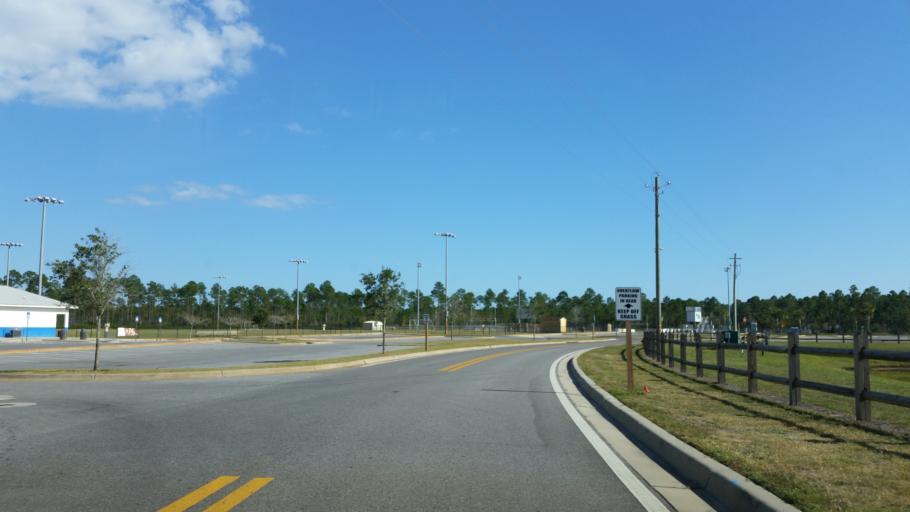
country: US
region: Florida
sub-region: Escambia County
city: Myrtle Grove
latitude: 30.3866
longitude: -87.3945
